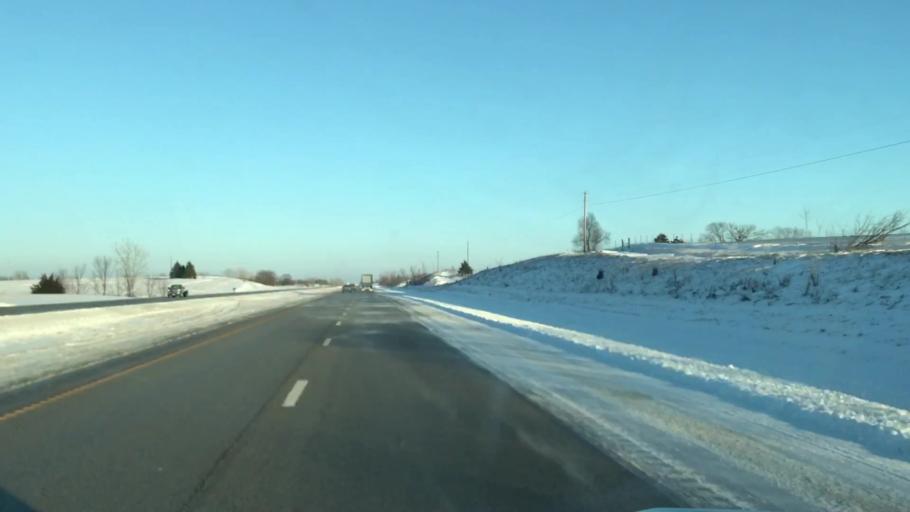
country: US
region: Missouri
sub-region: Clinton County
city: Gower
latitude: 39.7471
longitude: -94.6342
